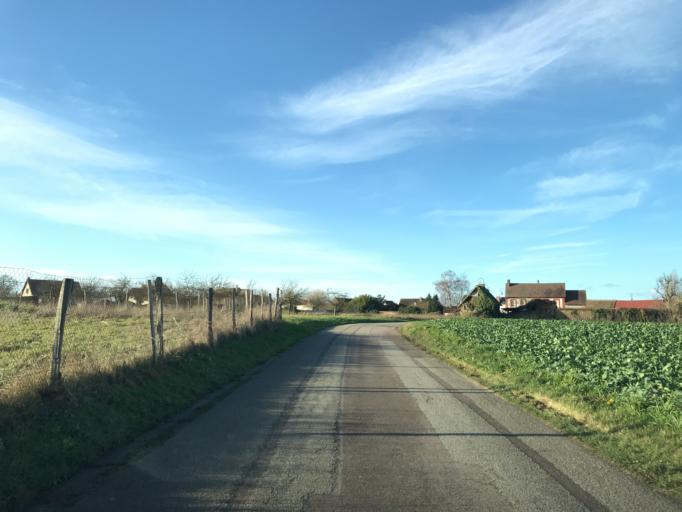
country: FR
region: Haute-Normandie
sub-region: Departement de l'Eure
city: Gravigny
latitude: 49.0769
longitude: 1.2263
